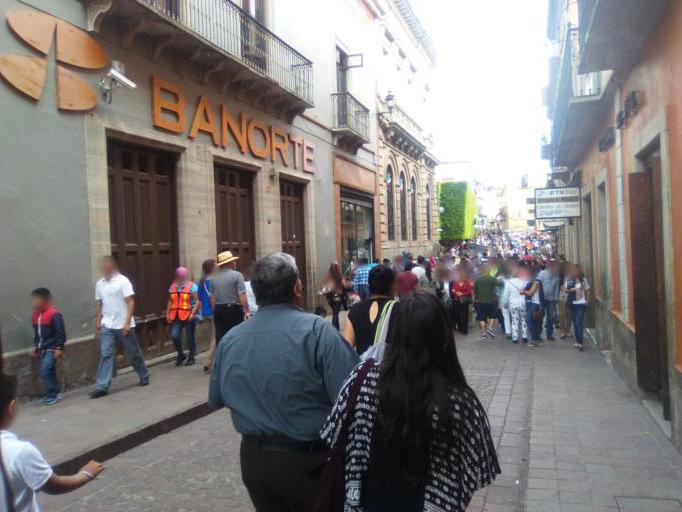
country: MX
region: Guanajuato
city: Guanajuato
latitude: 21.0161
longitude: -101.2535
